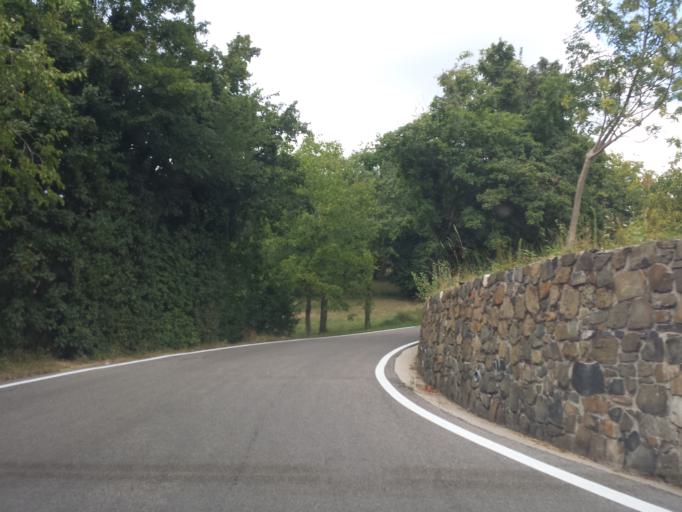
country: IT
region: Veneto
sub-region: Provincia di Vicenza
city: Valdagno
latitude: 45.6417
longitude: 11.3218
